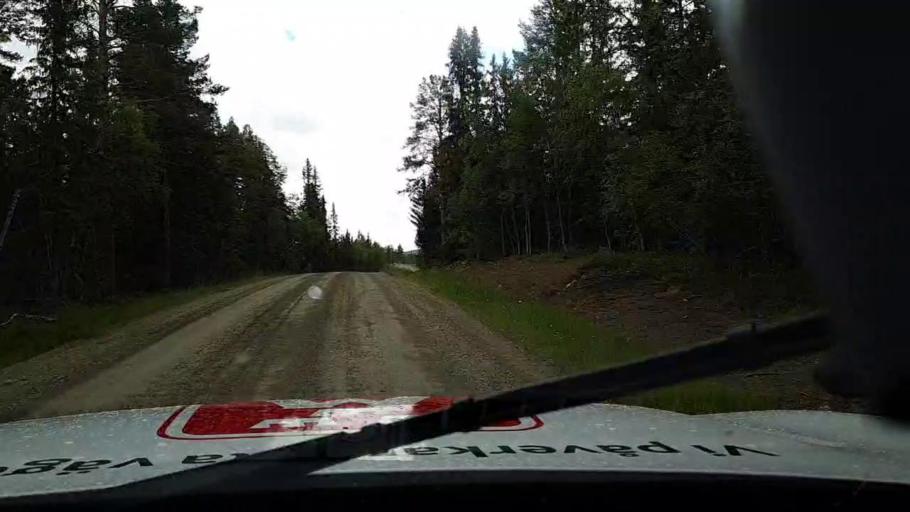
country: SE
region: Jaemtland
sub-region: Are Kommun
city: Jarpen
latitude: 62.6123
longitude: 13.2006
